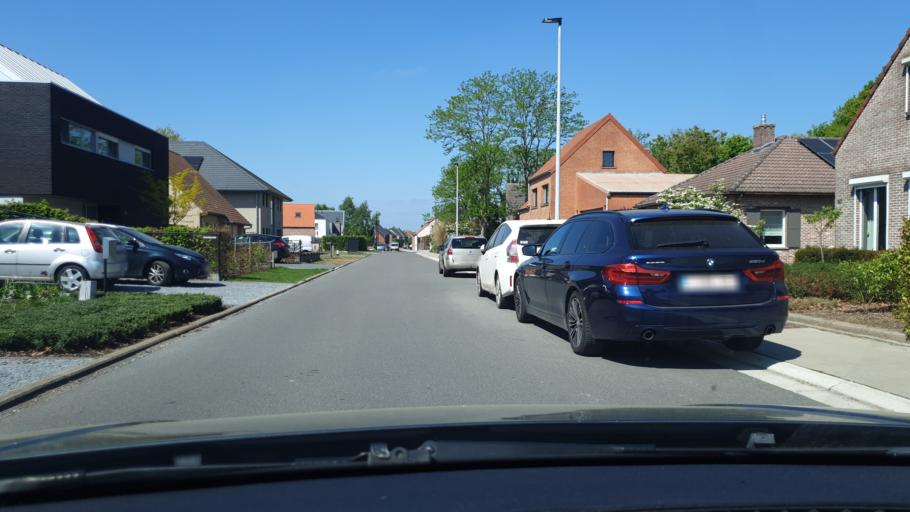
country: BE
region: Flanders
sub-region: Provincie Antwerpen
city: Geel
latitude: 51.1765
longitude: 4.9828
